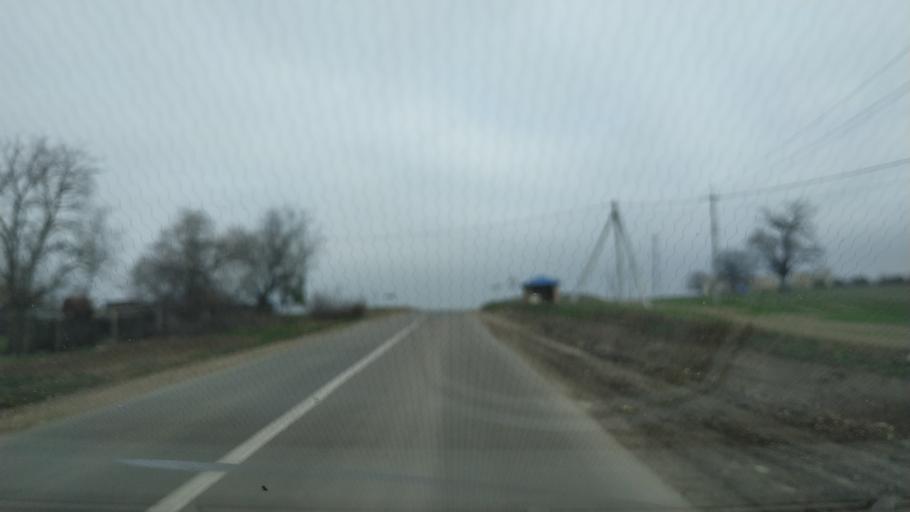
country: MD
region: Straseni
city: Taraclia
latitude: 45.9332
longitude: 28.5831
